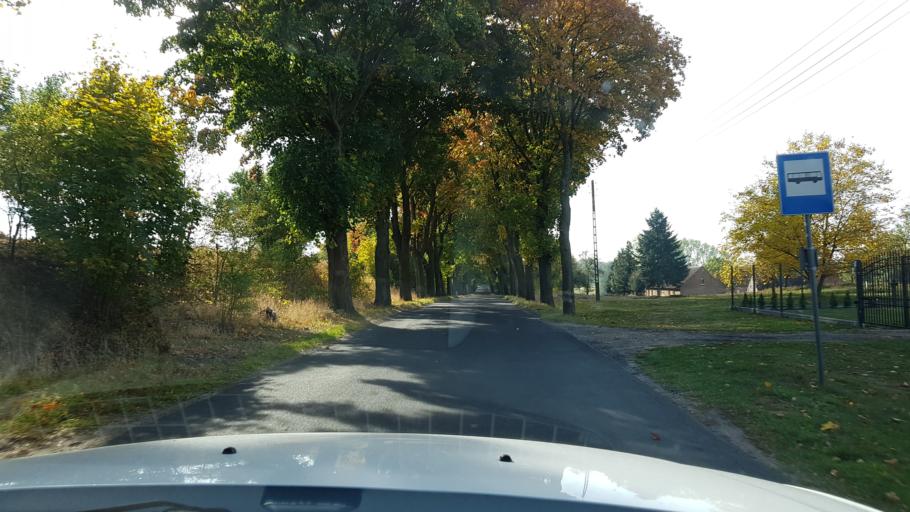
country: PL
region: West Pomeranian Voivodeship
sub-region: Powiat mysliborski
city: Nowogrodek Pomorski
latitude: 52.9470
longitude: 15.0965
